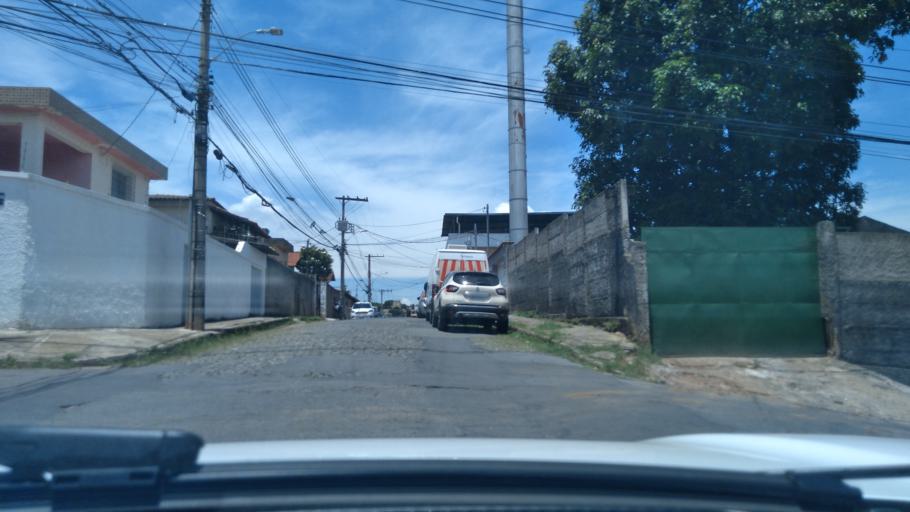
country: BR
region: Minas Gerais
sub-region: Contagem
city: Contagem
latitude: -19.9302
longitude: -43.9971
